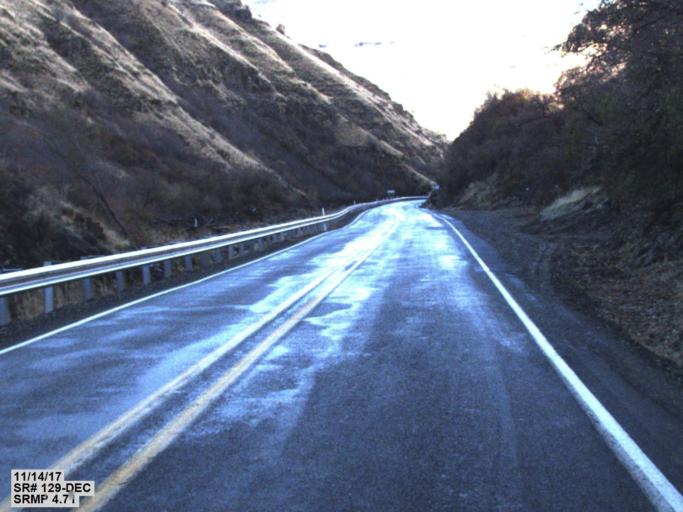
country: US
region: Washington
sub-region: Asotin County
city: Asotin
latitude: 46.0435
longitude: -117.2460
